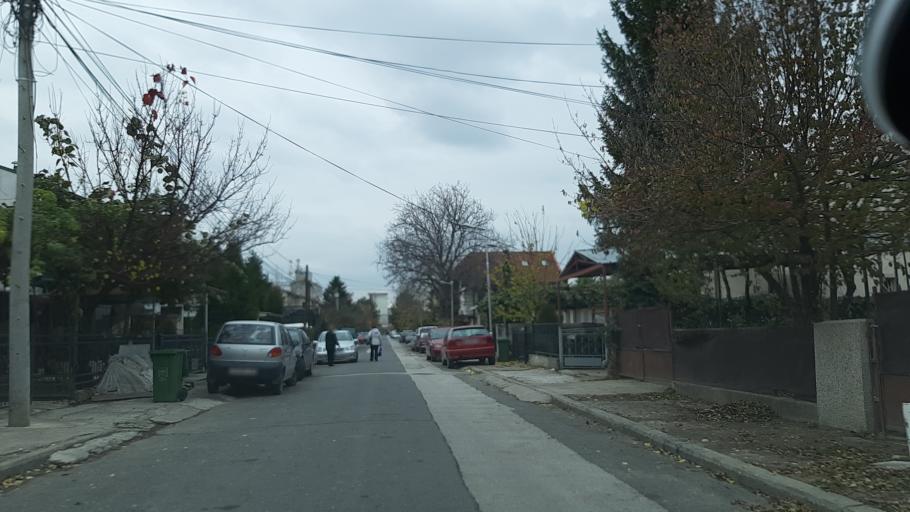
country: MK
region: Kisela Voda
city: Usje
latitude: 41.9740
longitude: 21.4679
